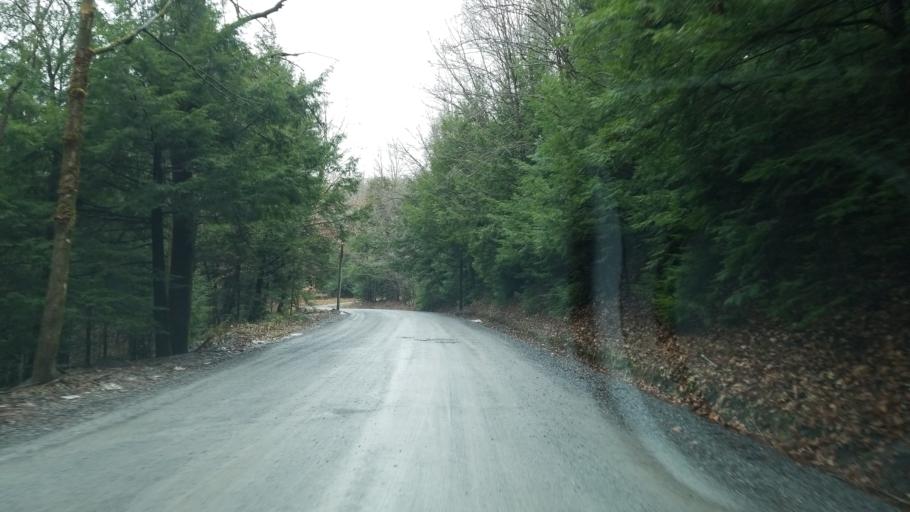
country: US
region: Pennsylvania
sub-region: Clearfield County
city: Treasure Lake
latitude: 41.0837
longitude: -78.6597
